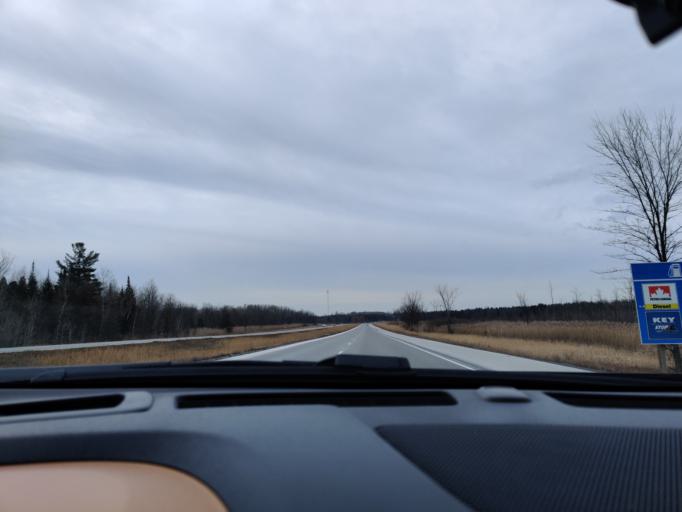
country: CA
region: Ontario
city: Cornwall
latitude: 45.0716
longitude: -74.6393
